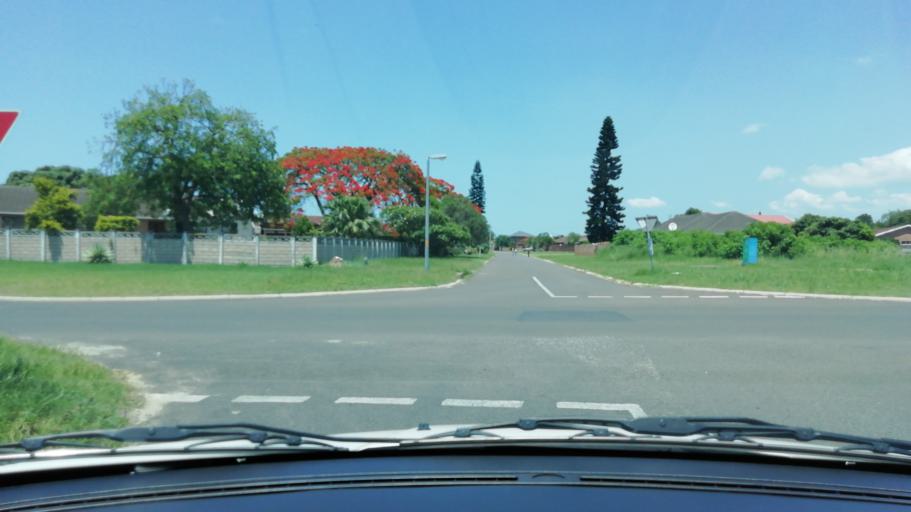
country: ZA
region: KwaZulu-Natal
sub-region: uThungulu District Municipality
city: Richards Bay
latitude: -28.7352
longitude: 32.0518
